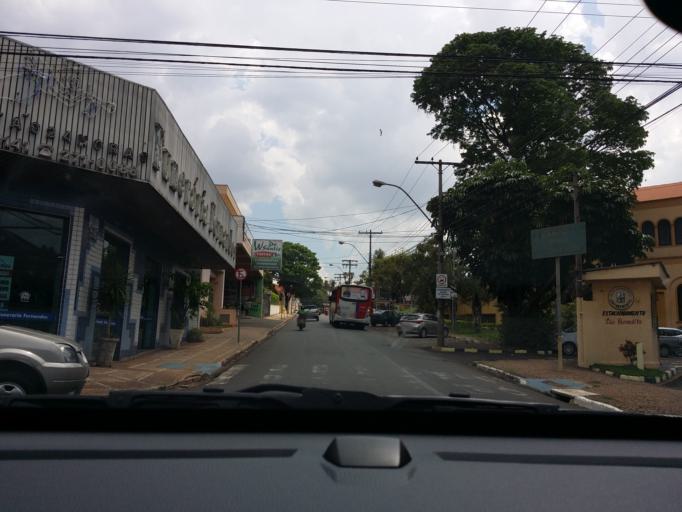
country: BR
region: Sao Paulo
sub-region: Sao Carlos
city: Sao Carlos
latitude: -22.0226
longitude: -47.8926
